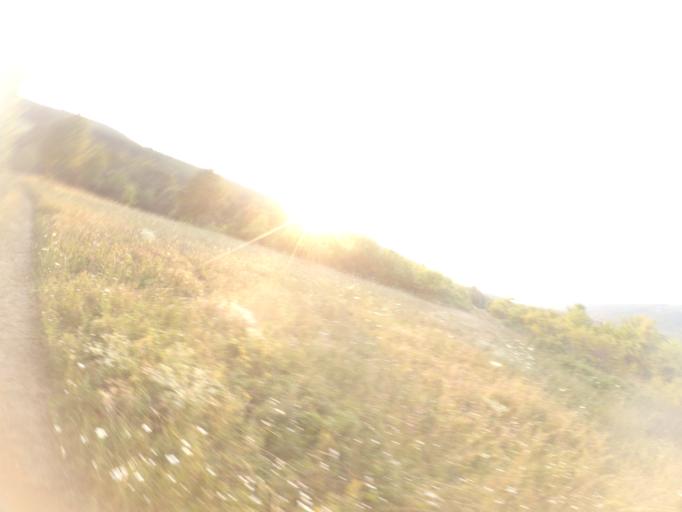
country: HU
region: Pest
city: Pilisszanto
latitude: 47.6676
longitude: 18.8680
